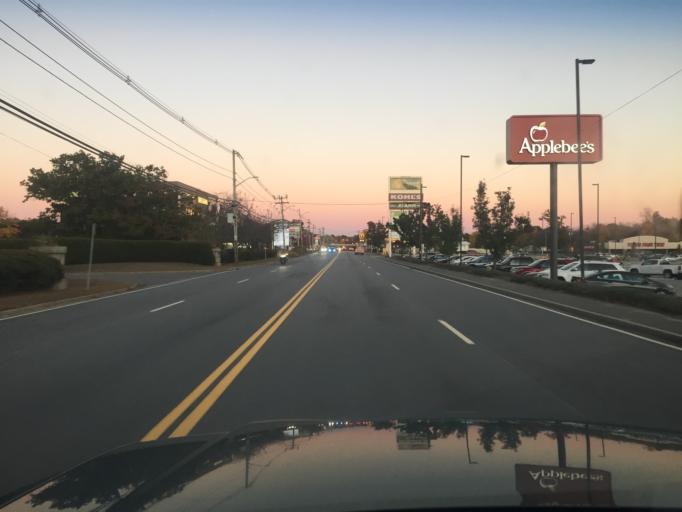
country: US
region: Massachusetts
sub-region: Worcester County
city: Milford
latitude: 42.1483
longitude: -71.4919
